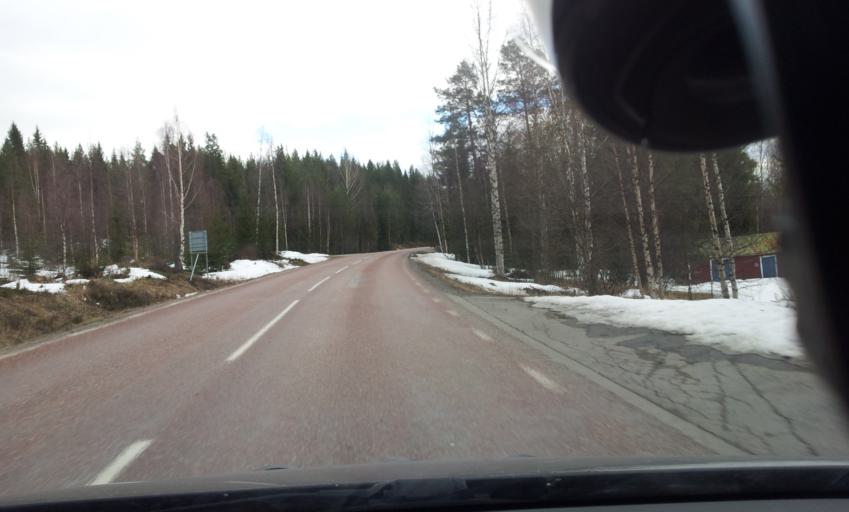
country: SE
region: Vaesternorrland
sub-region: Ange Kommun
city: Ange
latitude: 62.1526
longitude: 15.6806
